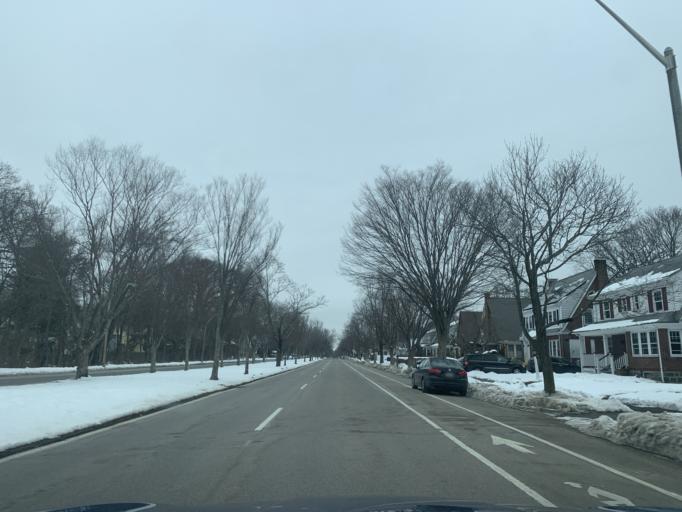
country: US
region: Massachusetts
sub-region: Norfolk County
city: Milton
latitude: 42.2538
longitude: -71.0935
